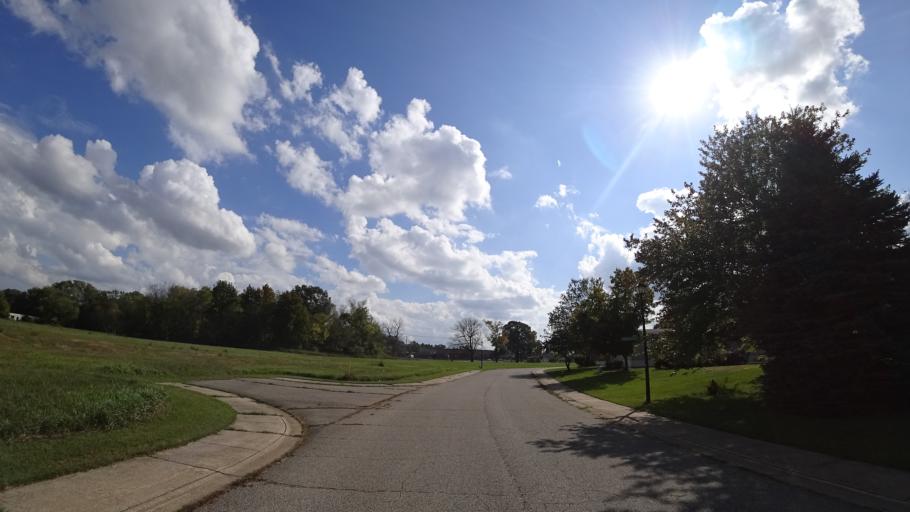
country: US
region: Michigan
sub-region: Saint Joseph County
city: Three Rivers
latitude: 41.9563
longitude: -85.6182
